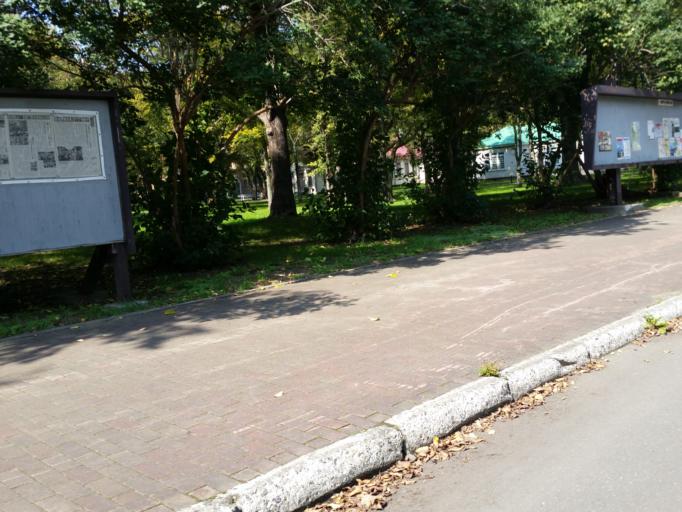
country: JP
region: Hokkaido
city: Sapporo
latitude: 43.0702
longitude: 141.3433
